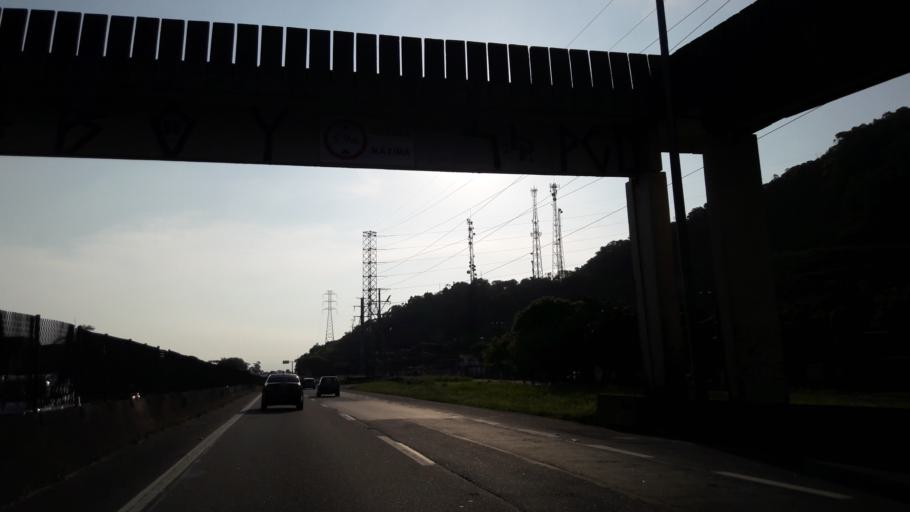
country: BR
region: Sao Paulo
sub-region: Mongagua
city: Mongagua
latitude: -24.0972
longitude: -46.6292
